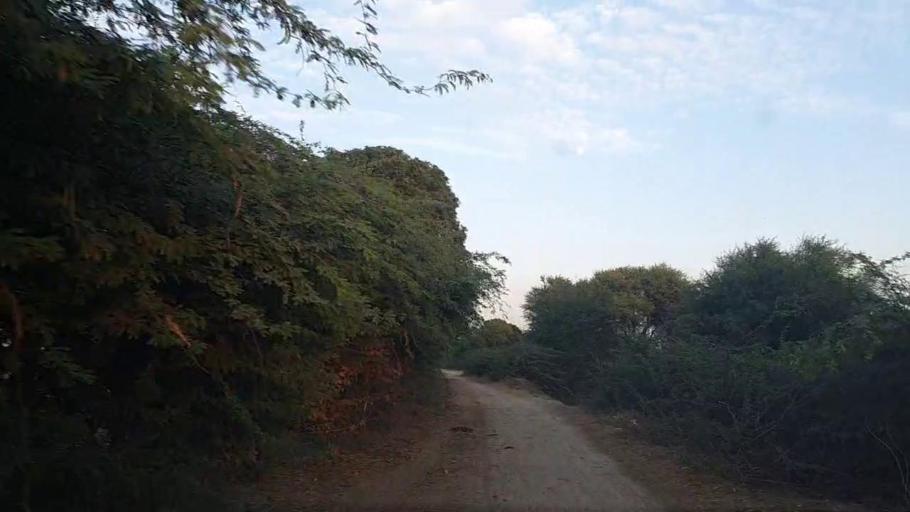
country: PK
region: Sindh
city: Thatta
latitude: 24.7915
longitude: 67.9220
